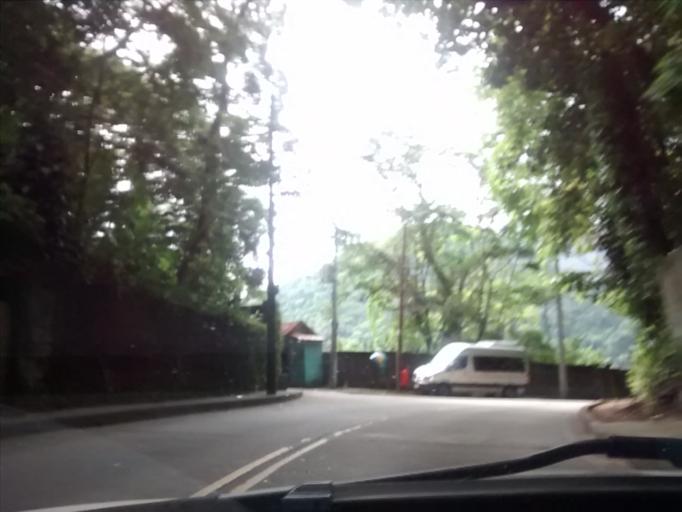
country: BR
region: Rio de Janeiro
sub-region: Rio De Janeiro
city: Rio de Janeiro
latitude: -22.9745
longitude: -43.2813
